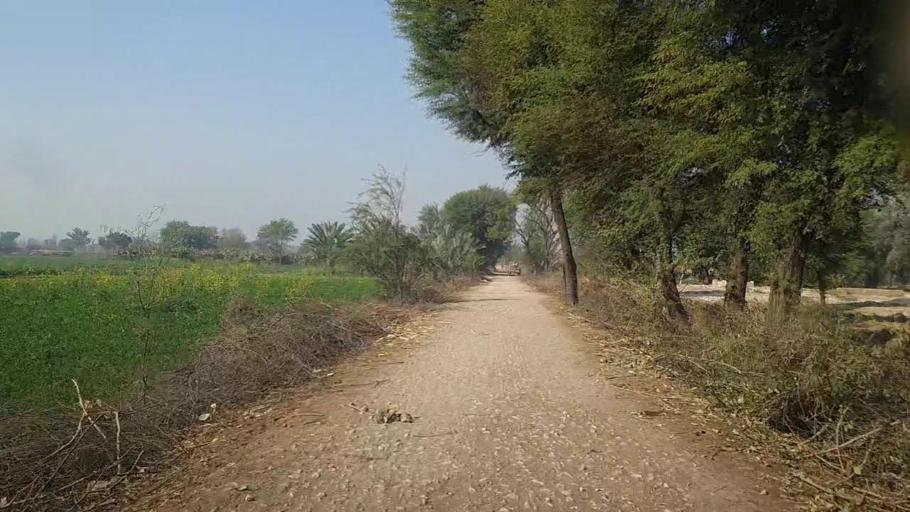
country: PK
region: Sindh
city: Karaundi
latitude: 26.8459
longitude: 68.3751
